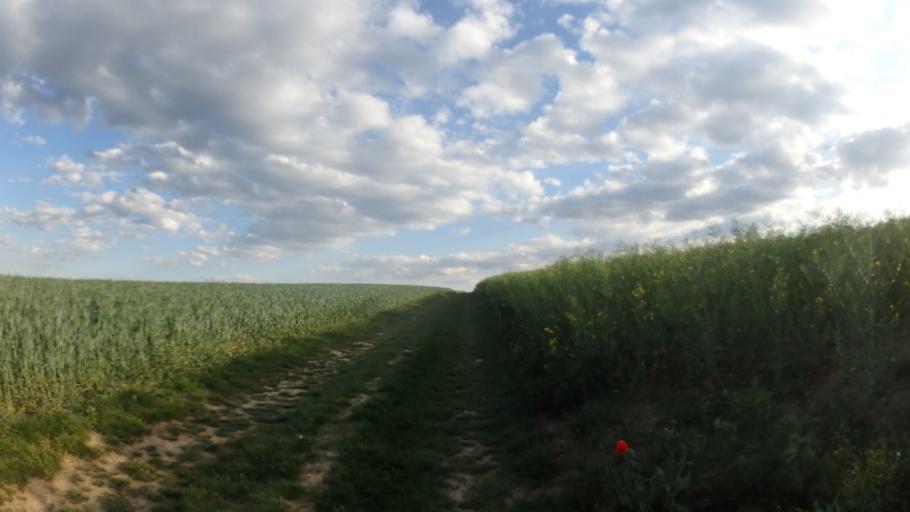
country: CZ
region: South Moravian
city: Moravany
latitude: 49.1401
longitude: 16.5921
